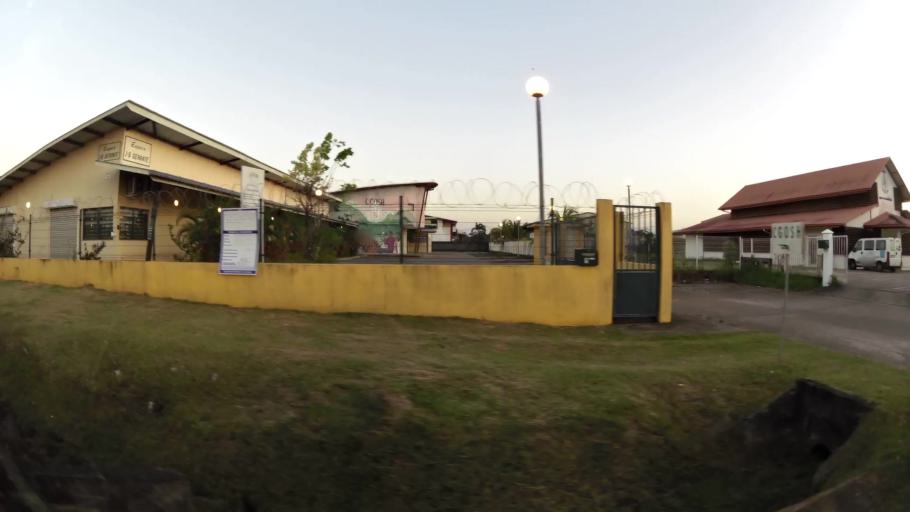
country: GF
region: Guyane
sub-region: Guyane
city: Cayenne
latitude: 4.9201
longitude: -52.3141
